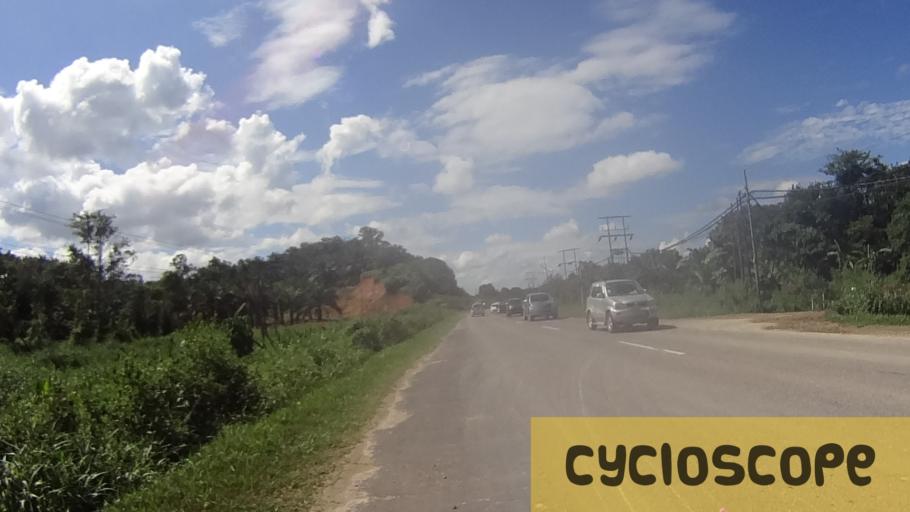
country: MY
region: Sabah
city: Beaufort
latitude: 5.3218
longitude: 115.7132
